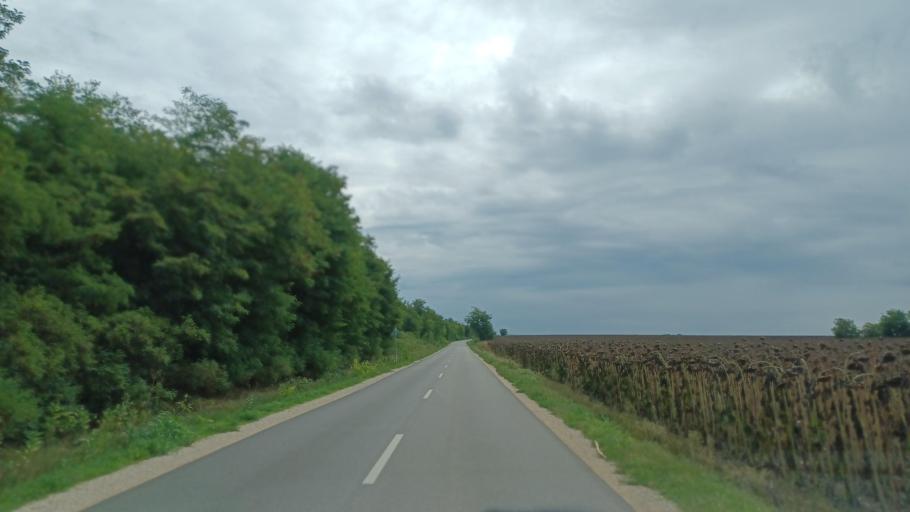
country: HU
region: Tolna
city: Szentgalpuszta
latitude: 46.4164
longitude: 18.6118
